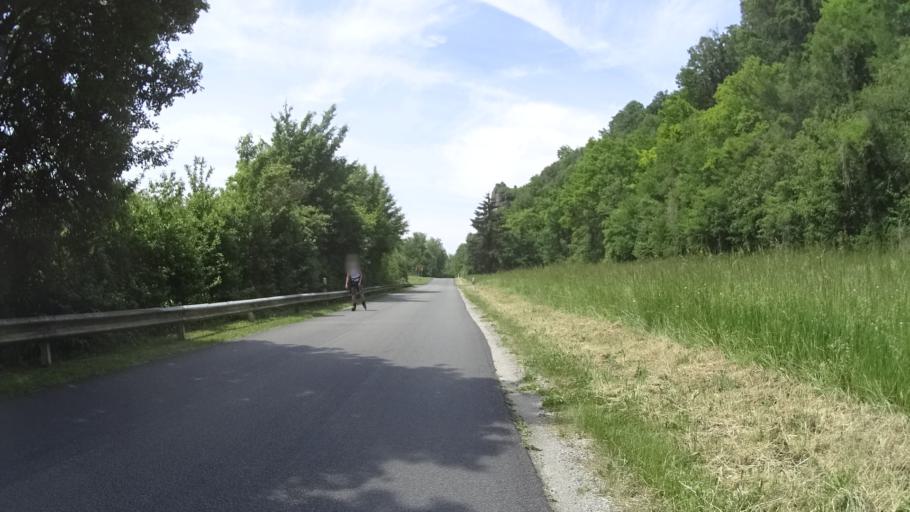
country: DE
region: Bavaria
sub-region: Lower Bavaria
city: Bad Abbach
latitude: 48.9519
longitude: 12.0063
